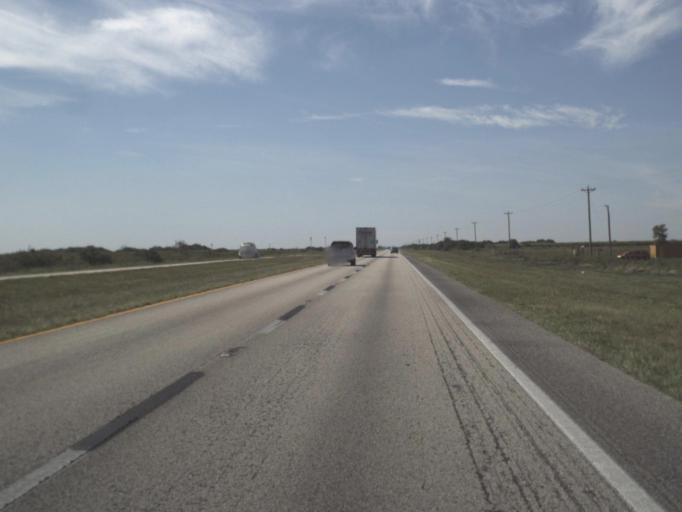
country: US
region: Florida
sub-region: Glades County
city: Moore Haven
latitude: 26.8339
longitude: -81.1590
